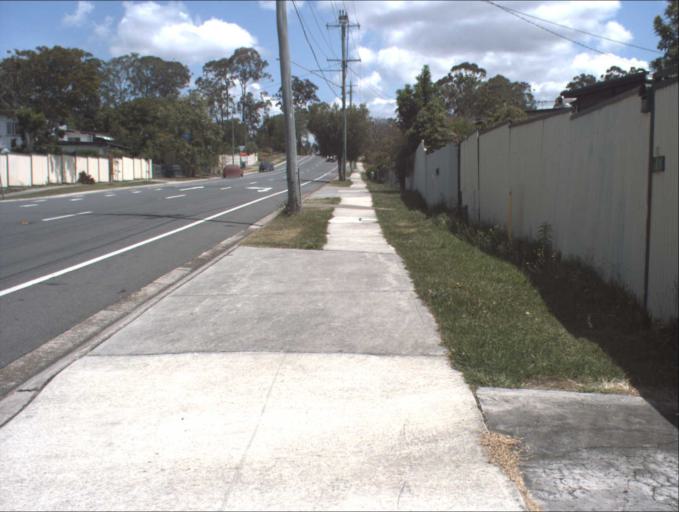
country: AU
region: Queensland
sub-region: Logan
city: Woodridge
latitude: -27.6201
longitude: 153.1001
